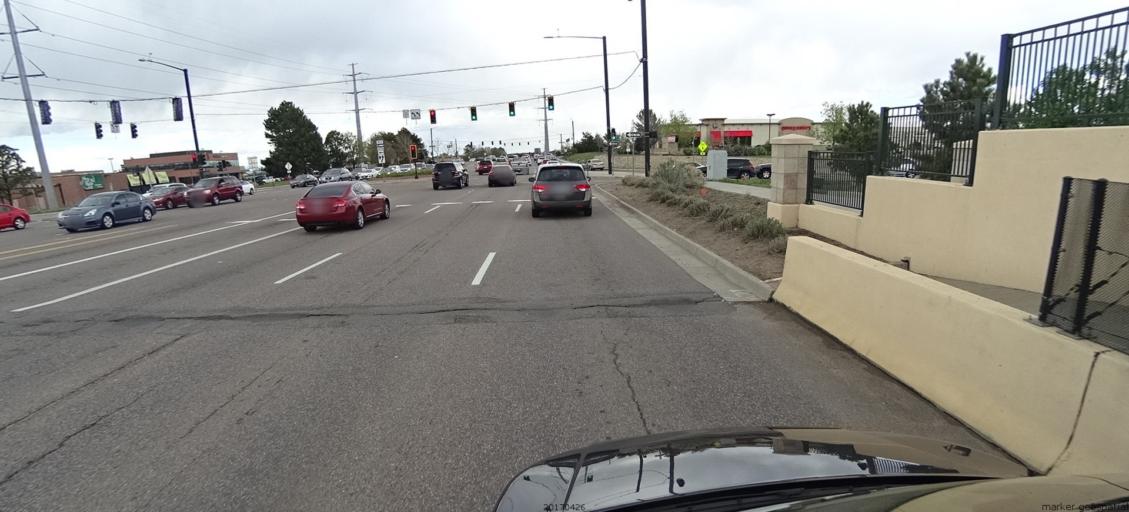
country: US
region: Colorado
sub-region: Douglas County
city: Acres Green
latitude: 39.5640
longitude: -104.9043
